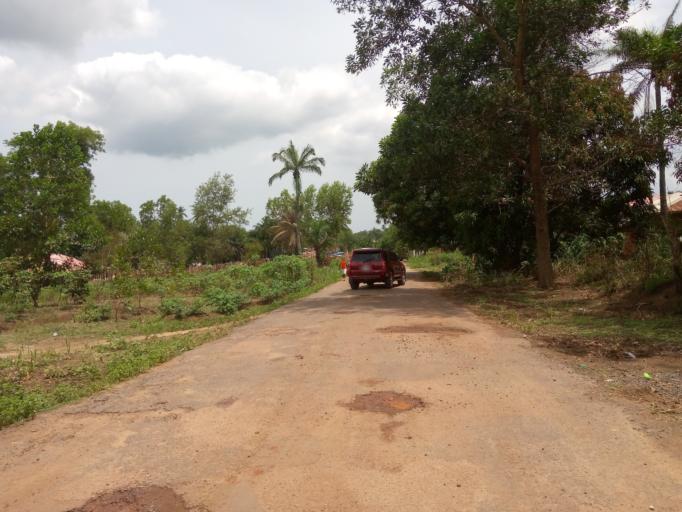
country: SL
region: Western Area
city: Waterloo
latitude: 8.3491
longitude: -12.9829
